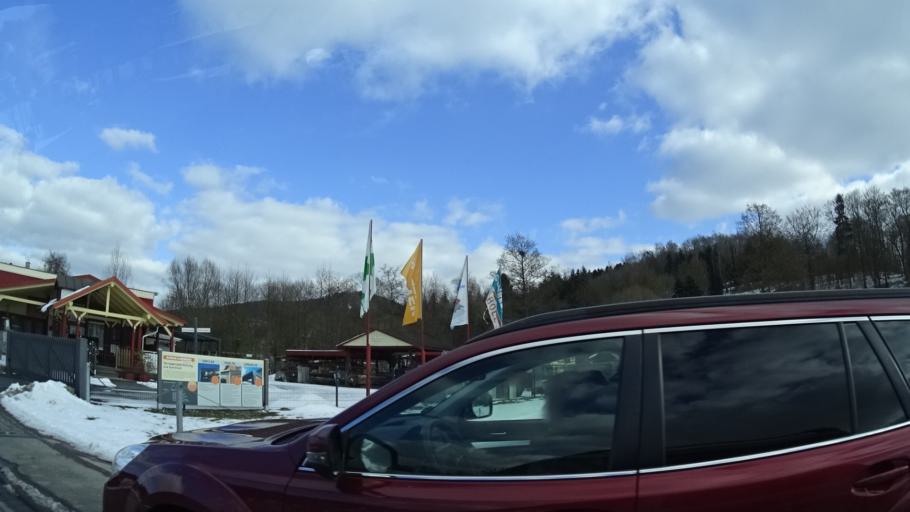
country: DE
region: Thuringia
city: Benshausen
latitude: 50.6377
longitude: 10.5903
